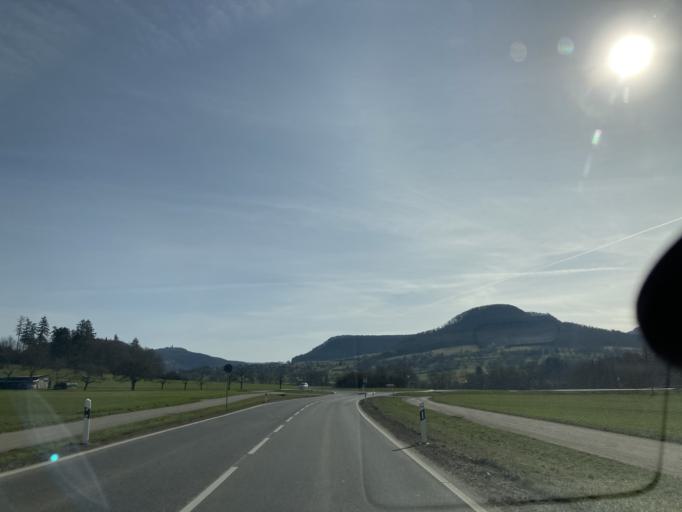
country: DE
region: Baden-Wuerttemberg
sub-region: Tuebingen Region
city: Nehren
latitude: 48.4086
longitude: 9.0790
